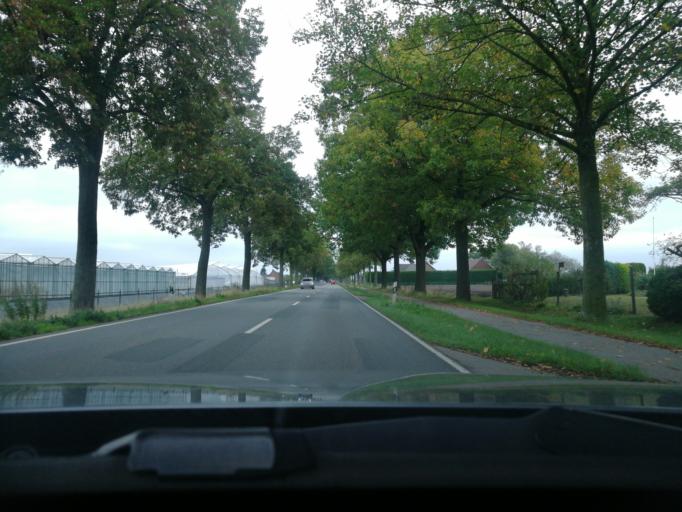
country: DE
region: North Rhine-Westphalia
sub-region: Regierungsbezirk Dusseldorf
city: Kevelaer
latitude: 51.5436
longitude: 6.2468
